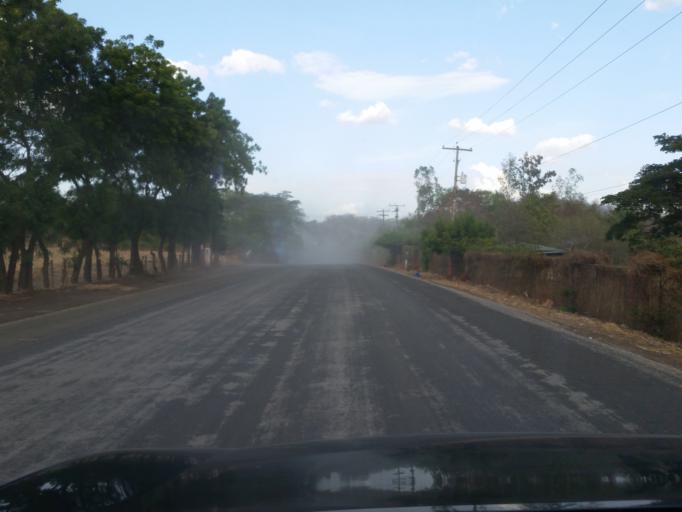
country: NI
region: Managua
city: Carlos Fonseca Amador
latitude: 12.0635
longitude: -86.4681
